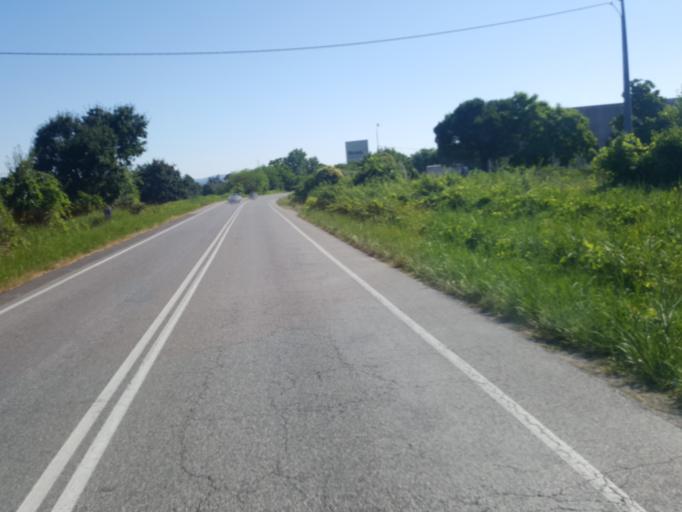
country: IT
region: The Marches
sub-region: Provincia di Pesaro e Urbino
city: Montelabbate
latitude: 43.8438
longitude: 12.7717
